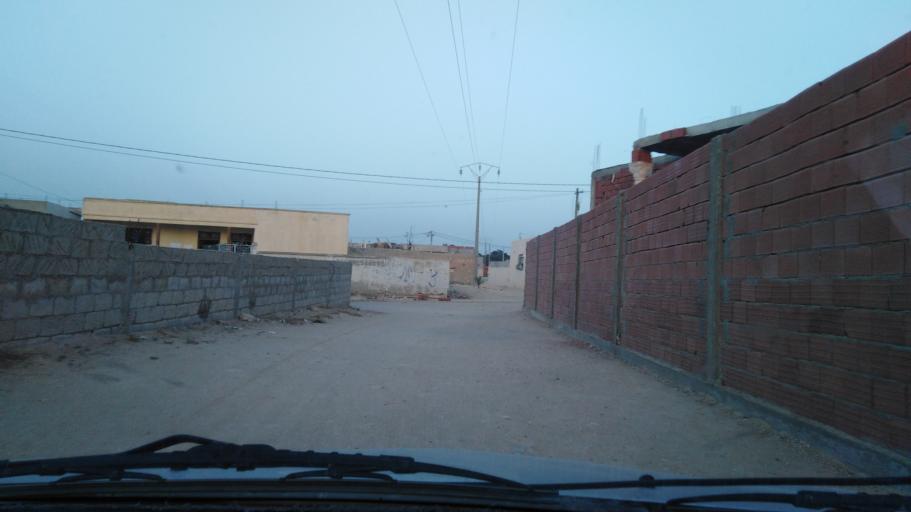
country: TN
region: Qabis
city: Gabes
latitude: 33.9533
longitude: 9.9960
